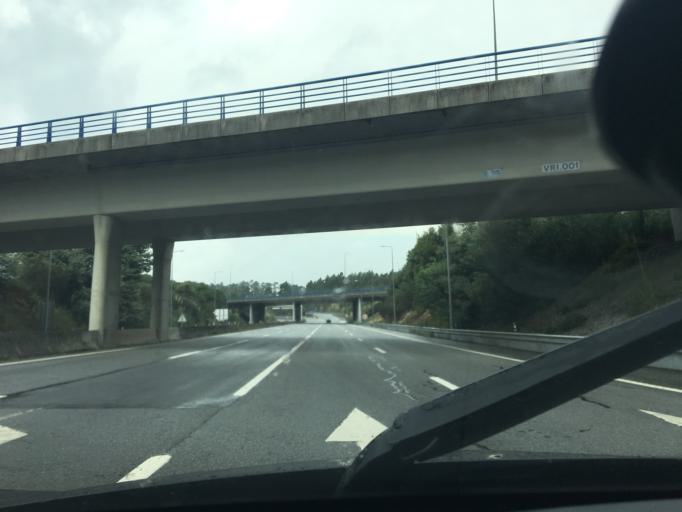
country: PT
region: Porto
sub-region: Matosinhos
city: Santa Cruz do Bispo
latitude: 41.2242
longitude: -8.6631
